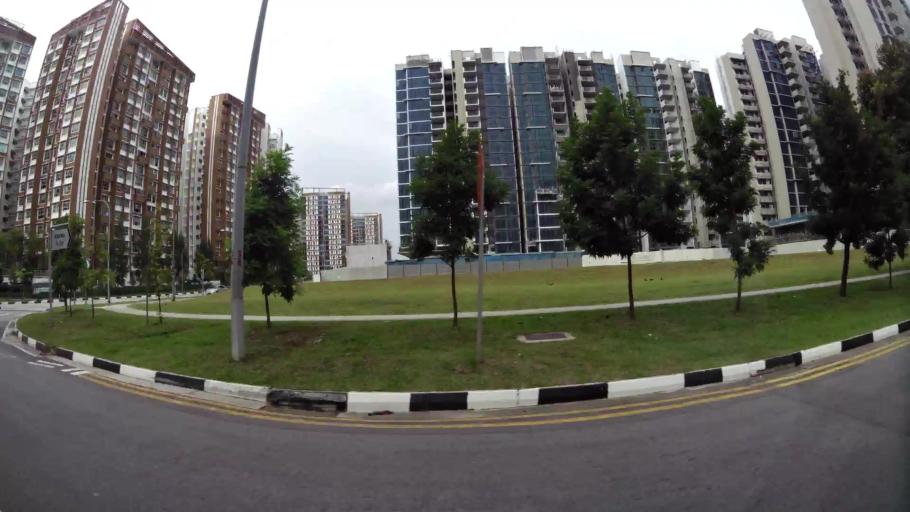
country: MY
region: Johor
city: Kampung Pasir Gudang Baru
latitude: 1.4006
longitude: 103.9153
